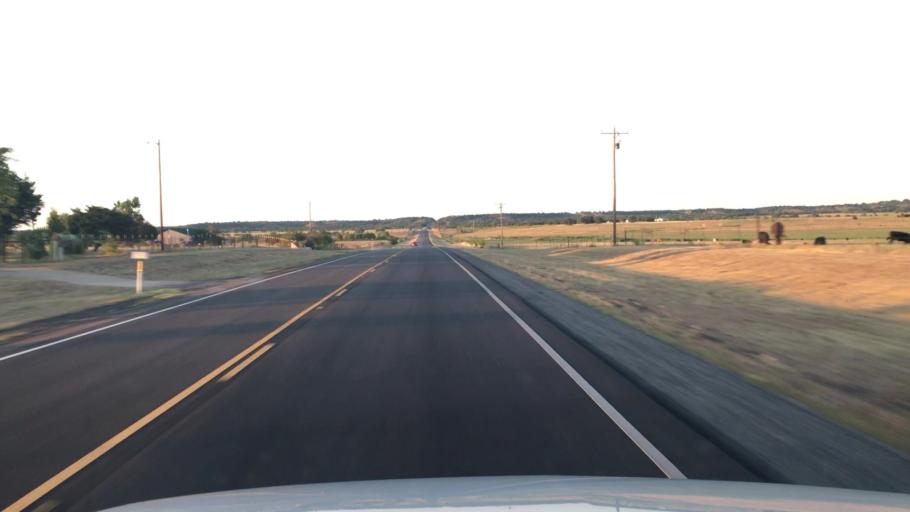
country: US
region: Texas
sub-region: Hamilton County
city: Hico
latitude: 32.0734
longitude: -97.9854
